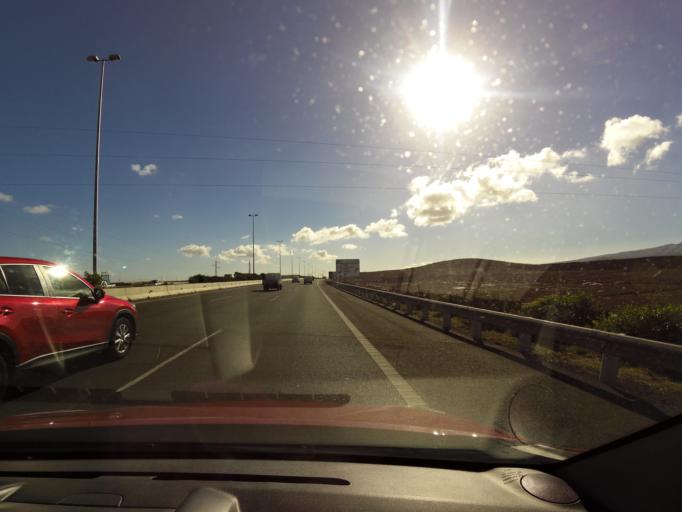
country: ES
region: Canary Islands
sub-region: Provincia de Las Palmas
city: Cruce de Arinaga
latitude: 27.8841
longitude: -15.4106
